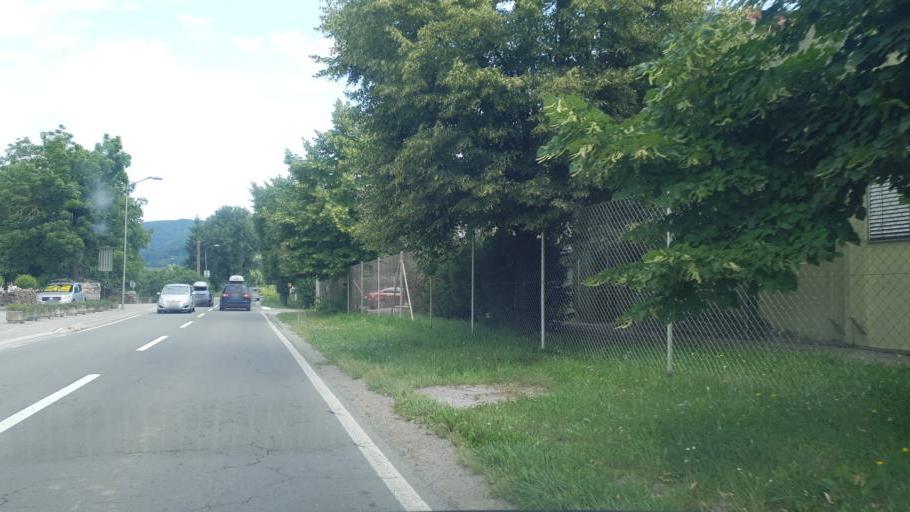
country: SI
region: Ilirska Bistrica
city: Ilirska Bistrica
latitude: 45.5553
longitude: 14.2413
